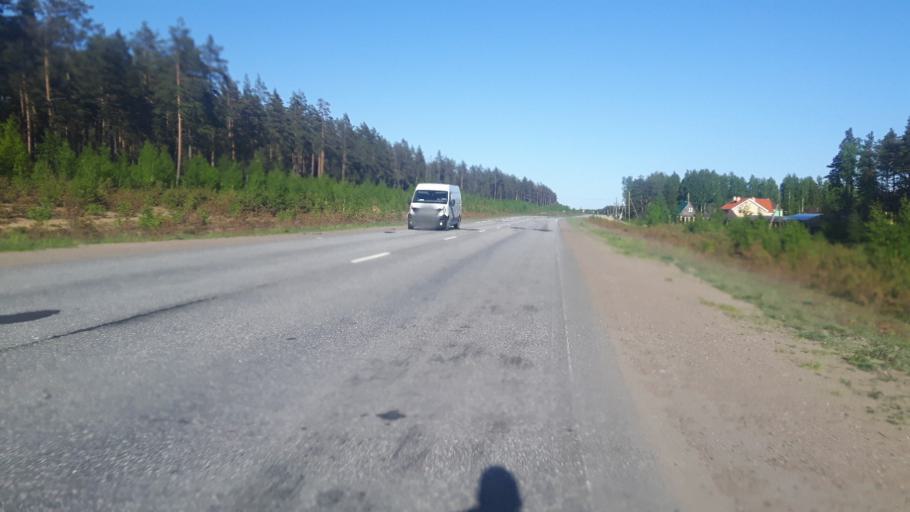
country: RU
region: Leningrad
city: Sosnovyy Bor
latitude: 60.1693
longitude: 29.2035
